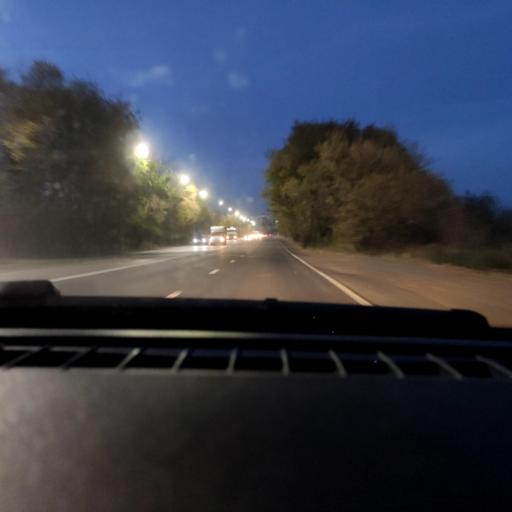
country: RU
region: Voronezj
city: Maslovka
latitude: 51.6249
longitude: 39.2814
